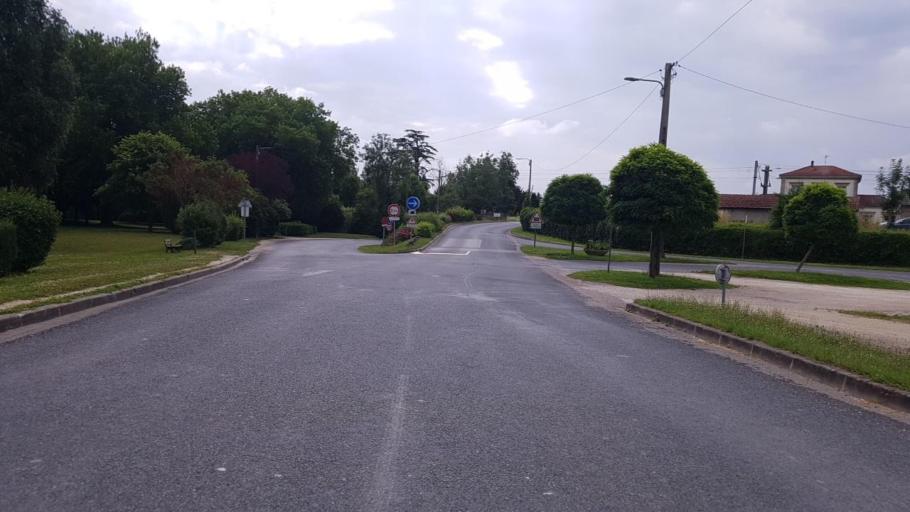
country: FR
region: Champagne-Ardenne
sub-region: Departement de la Marne
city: Sermaize-les-Bains
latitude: 48.7875
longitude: 4.9060
